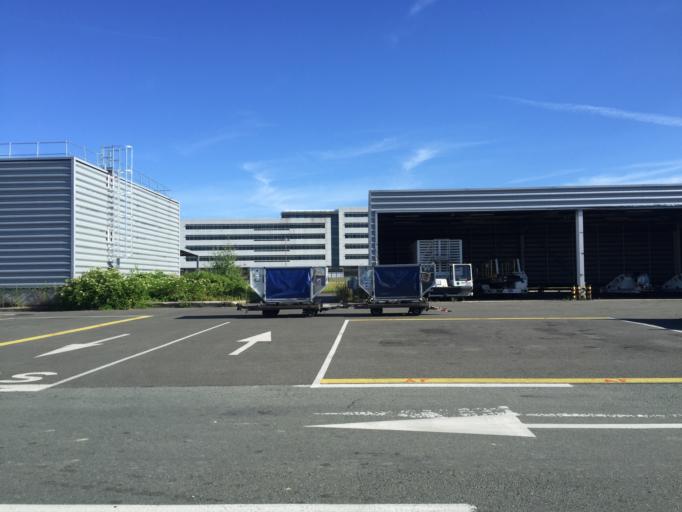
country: FR
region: Ile-de-France
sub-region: Departement du Val-d'Oise
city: Roissy-en-France
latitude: 49.0075
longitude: 2.5668
